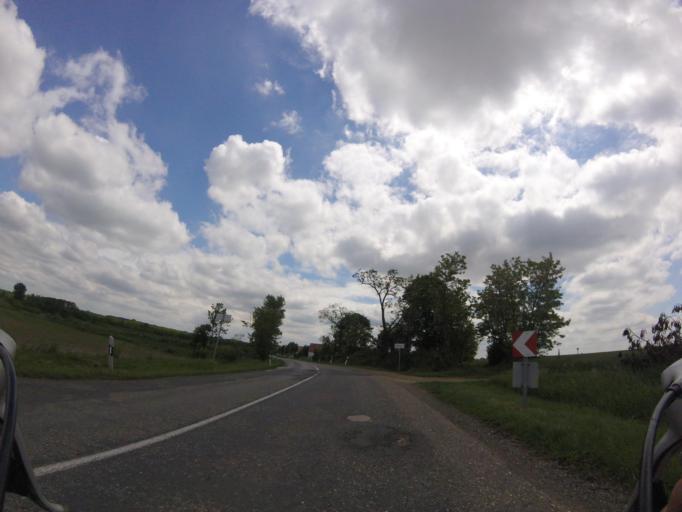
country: HU
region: Fejer
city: Sarosd
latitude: 47.0501
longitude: 18.6307
